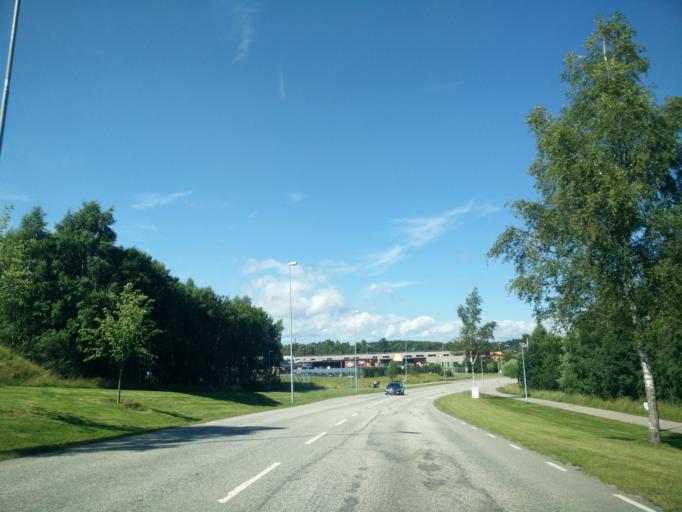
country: SE
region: Vaesternorrland
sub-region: Haernoesands Kommun
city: Haernoesand
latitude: 62.6279
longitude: 17.9150
